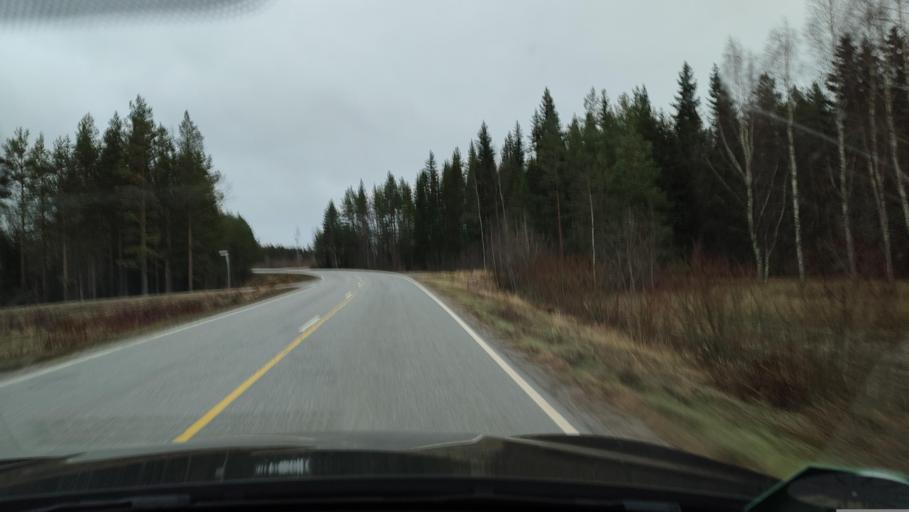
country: FI
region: Southern Ostrobothnia
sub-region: Suupohja
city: Karijoki
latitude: 62.2356
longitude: 21.7528
